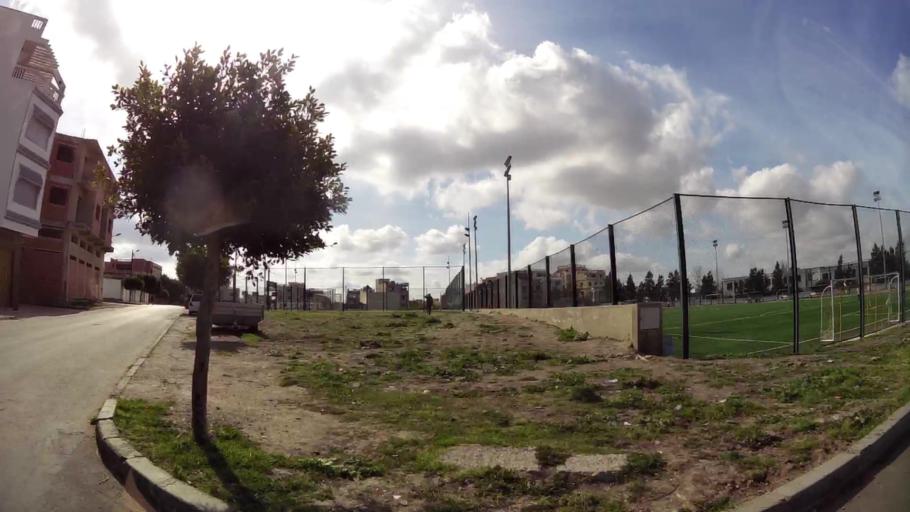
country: MA
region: Tanger-Tetouan
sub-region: Tanger-Assilah
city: Tangier
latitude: 35.7705
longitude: -5.7739
